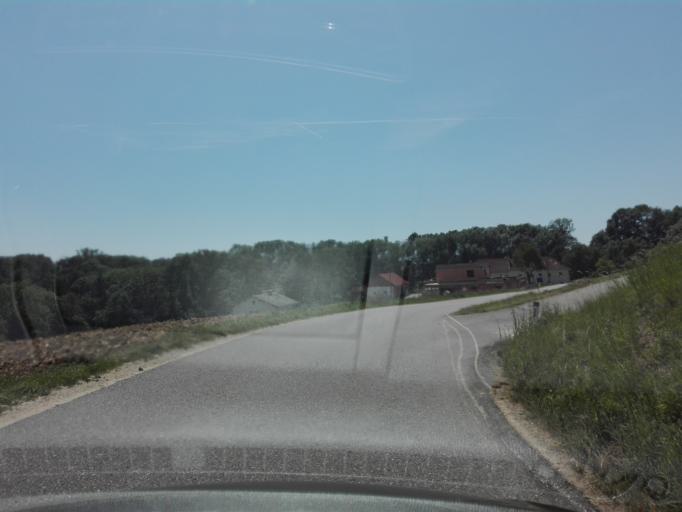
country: AT
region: Upper Austria
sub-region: Politischer Bezirk Urfahr-Umgebung
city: Steyregg
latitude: 48.2999
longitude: 14.3881
